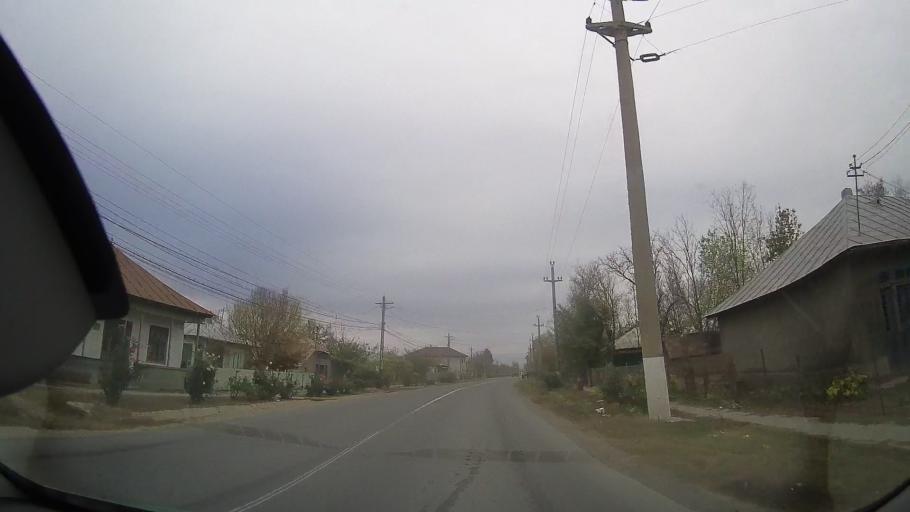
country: RO
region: Ialomita
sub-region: Comuna Grivita
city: Grivita
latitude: 44.7354
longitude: 27.2911
